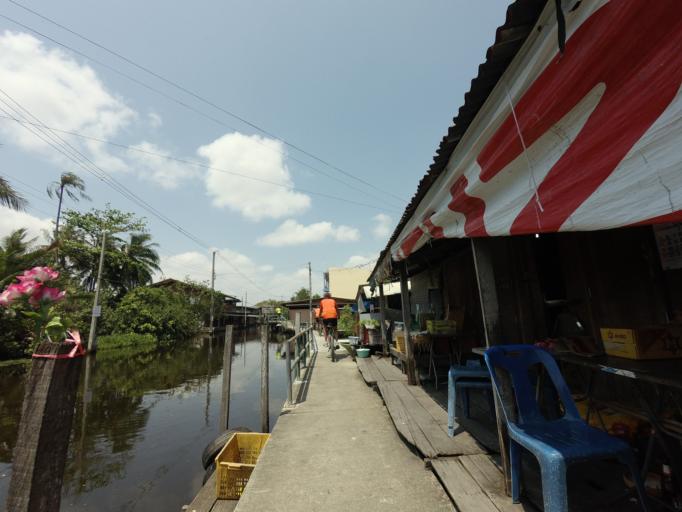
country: TH
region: Bangkok
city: Chom Thong
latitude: 13.6514
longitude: 100.4718
